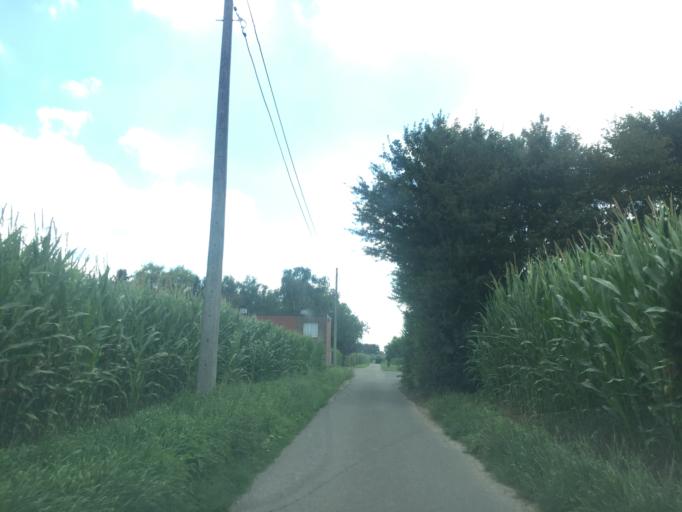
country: BE
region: Flanders
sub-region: Provincie West-Vlaanderen
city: Kortemark
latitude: 51.0005
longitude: 3.0402
